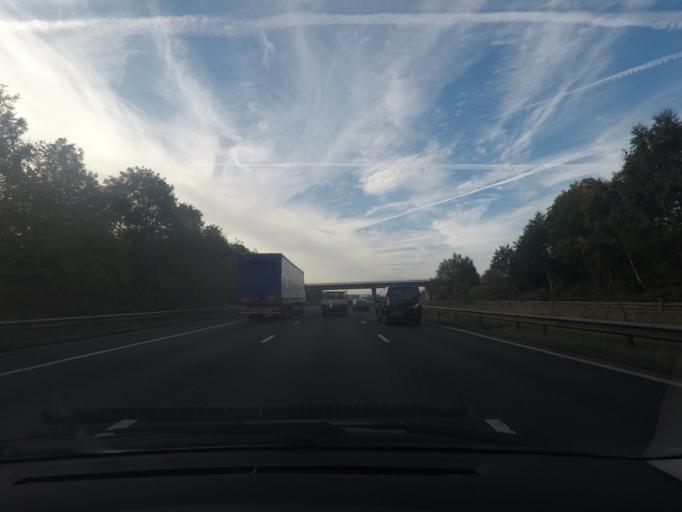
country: GB
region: England
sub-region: Barnsley
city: Darton
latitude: 53.5809
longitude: -1.5366
